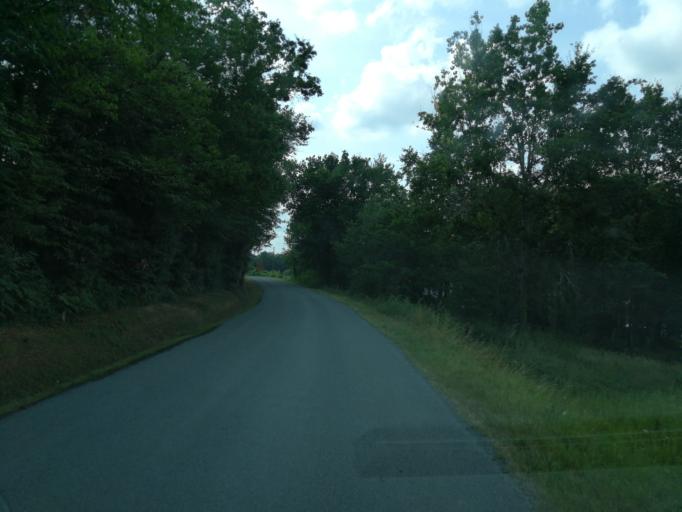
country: FR
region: Aquitaine
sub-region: Departement du Lot-et-Garonne
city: Monsempron-Libos
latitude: 44.5423
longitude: 0.9185
